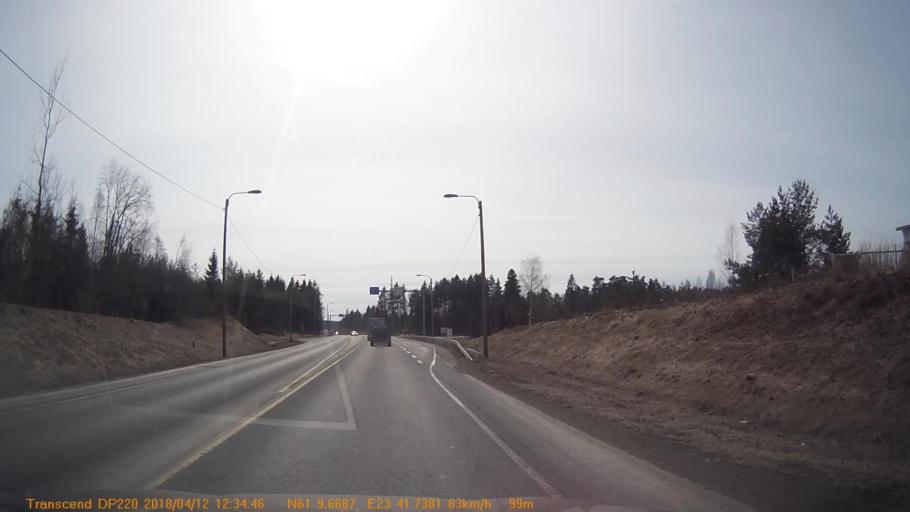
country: FI
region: Pirkanmaa
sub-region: Etelae-Pirkanmaa
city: Kylmaekoski
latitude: 61.1612
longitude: 23.6957
